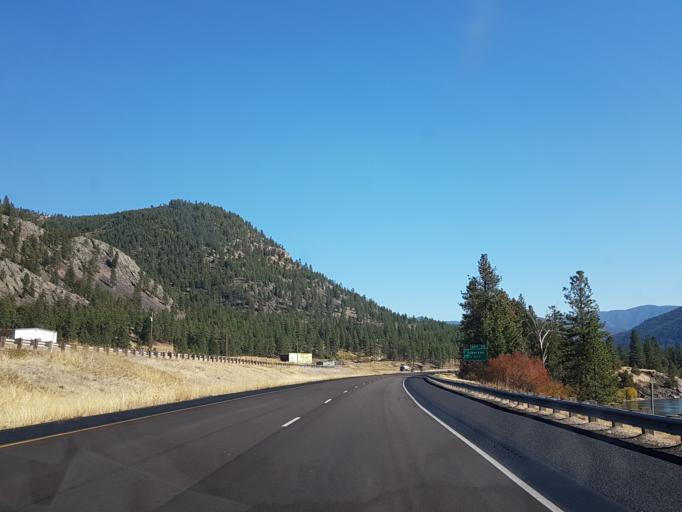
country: US
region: Montana
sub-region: Missoula County
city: Frenchtown
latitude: 47.0182
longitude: -114.5128
